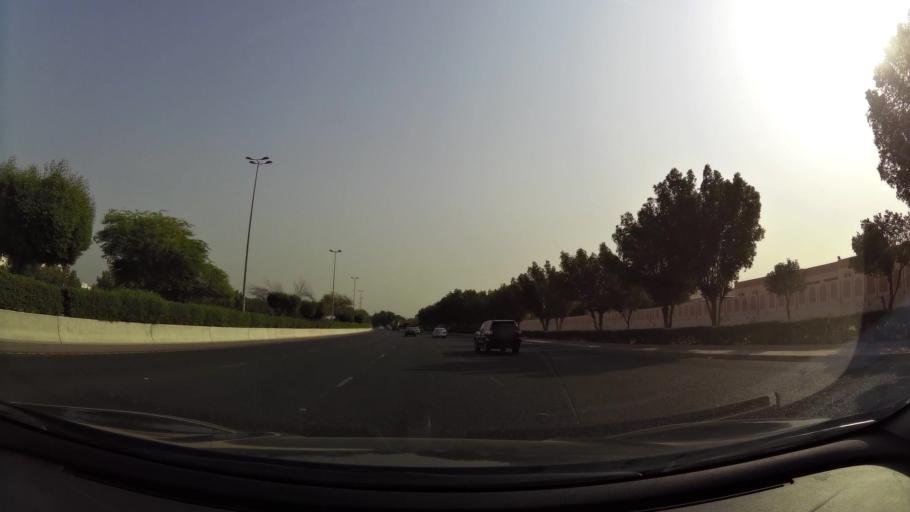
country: KW
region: Mubarak al Kabir
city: Sabah as Salim
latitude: 29.2358
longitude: 48.0717
